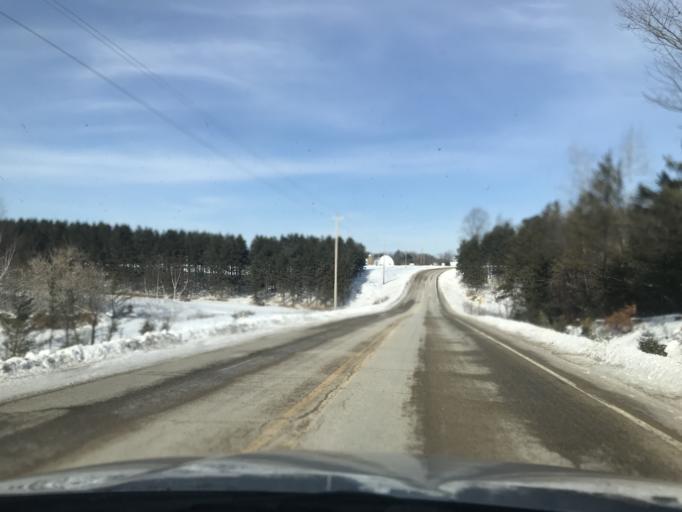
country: US
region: Wisconsin
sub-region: Oconto County
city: Oconto Falls
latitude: 45.1445
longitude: -88.1771
